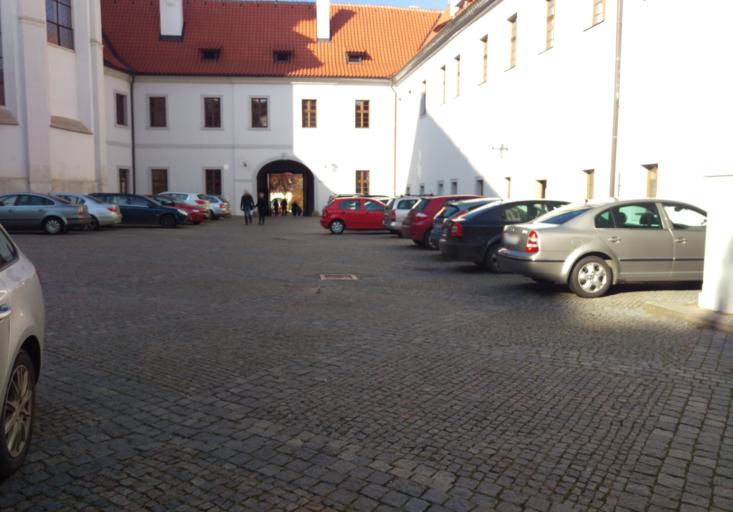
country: CZ
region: Praha
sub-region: Praha 1
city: Mala Strana
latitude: 50.0864
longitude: 14.3901
